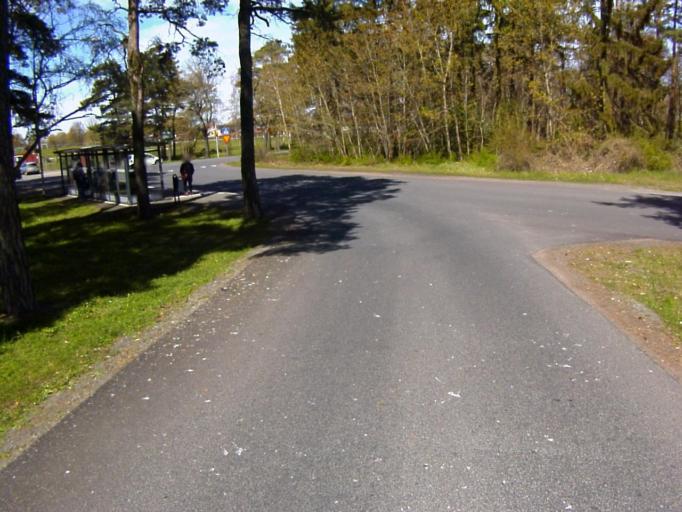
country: SE
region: Skane
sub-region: Kristianstads Kommun
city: Norra Asum
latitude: 55.9894
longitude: 14.1459
